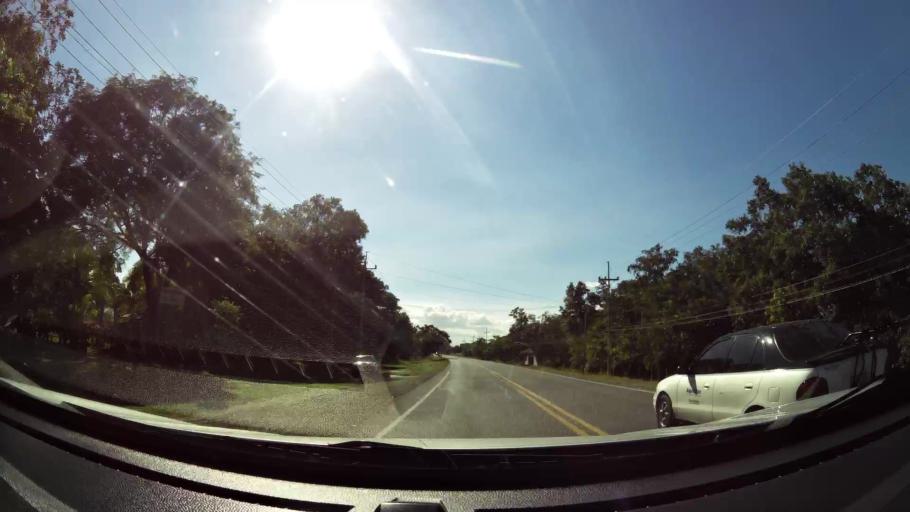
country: CR
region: Guanacaste
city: Liberia
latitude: 10.6120
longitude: -85.4964
